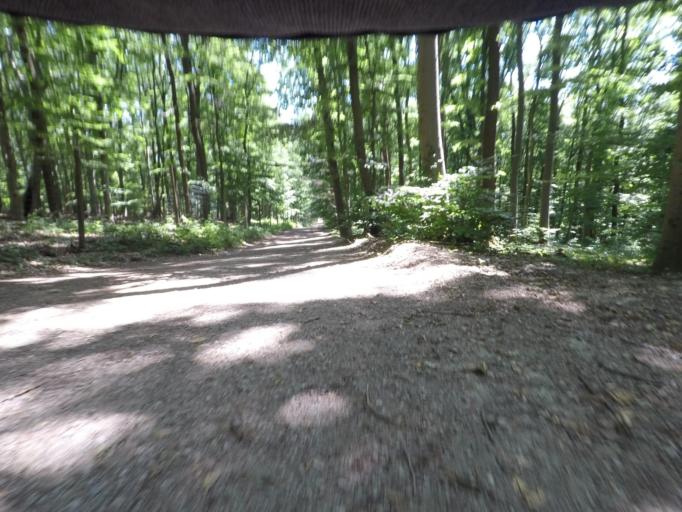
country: AT
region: Lower Austria
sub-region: Politischer Bezirk Modling
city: Perchtoldsdorf
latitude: 48.1778
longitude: 16.2486
